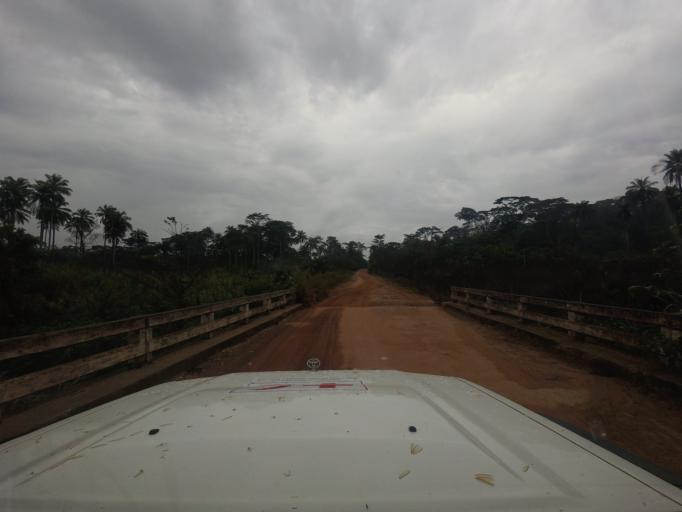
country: LR
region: Lofa
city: Voinjama
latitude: 8.3903
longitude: -9.8120
